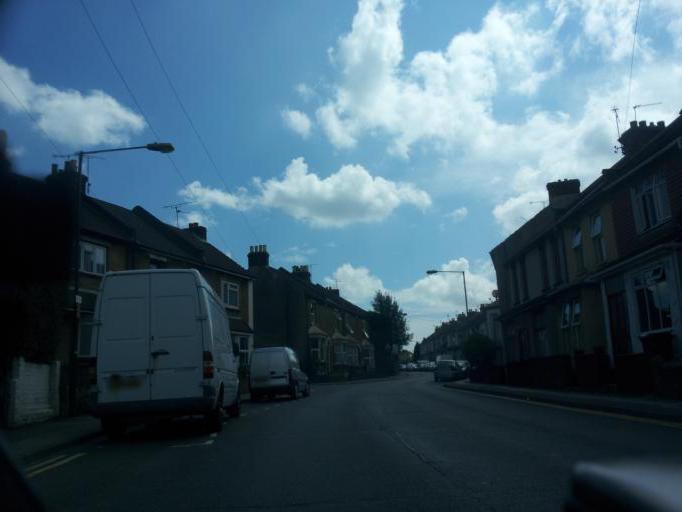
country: GB
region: England
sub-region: Kent
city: Gillingham
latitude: 51.3838
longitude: 0.5563
